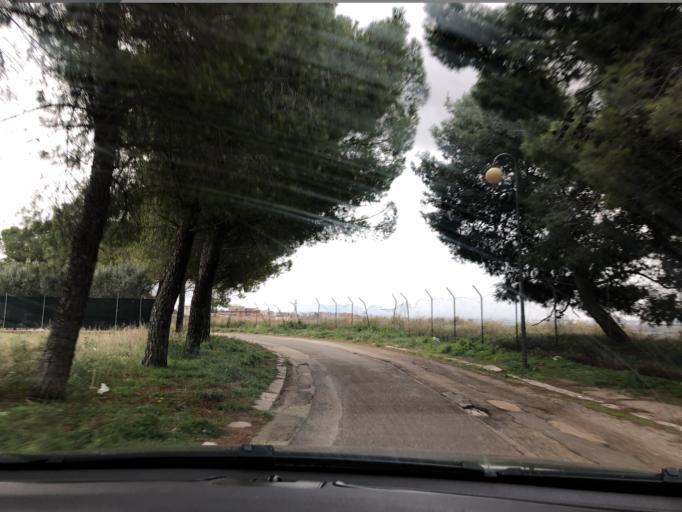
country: IT
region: Apulia
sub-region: Provincia di Foggia
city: Lucera
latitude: 41.5061
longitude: 15.3254
